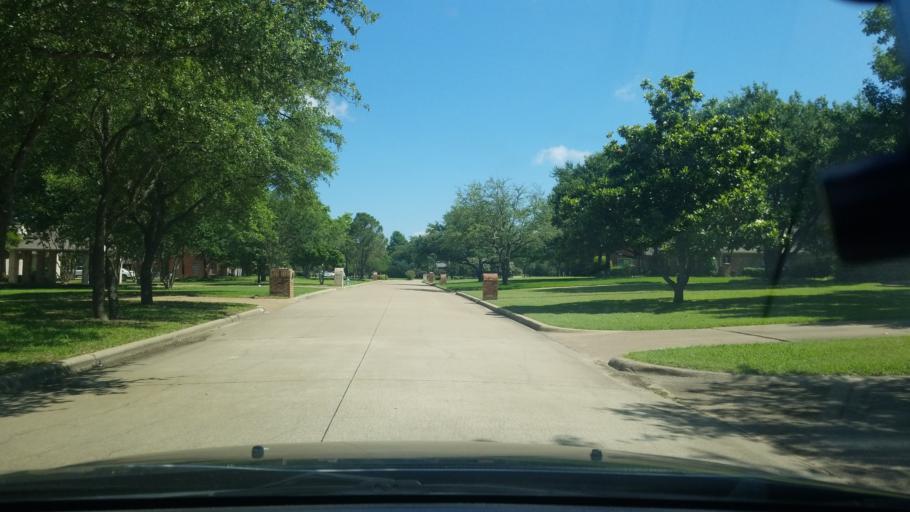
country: US
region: Texas
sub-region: Dallas County
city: Sunnyvale
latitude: 32.7991
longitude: -96.5891
